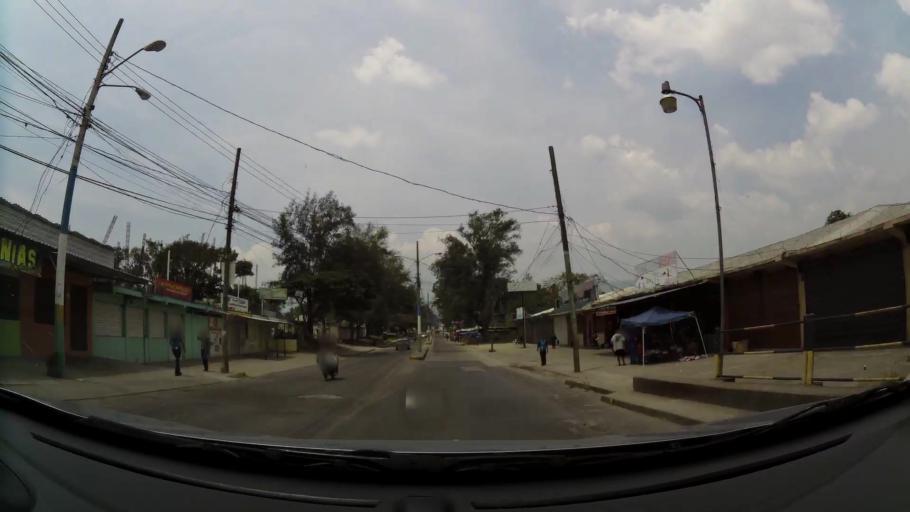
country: HN
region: Comayagua
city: Siguatepeque
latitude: 14.5918
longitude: -87.8323
